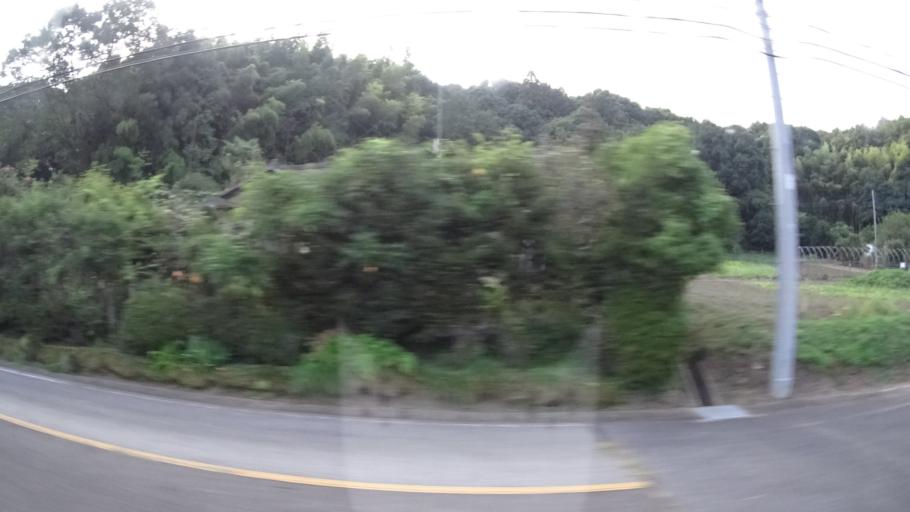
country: JP
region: Tochigi
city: Karasuyama
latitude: 36.5814
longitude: 140.1087
